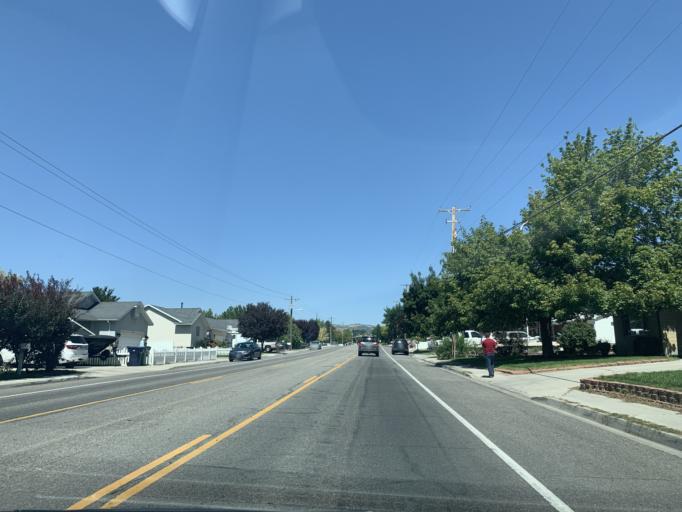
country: US
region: Utah
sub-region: Utah County
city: Lehi
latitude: 40.3951
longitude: -111.8301
